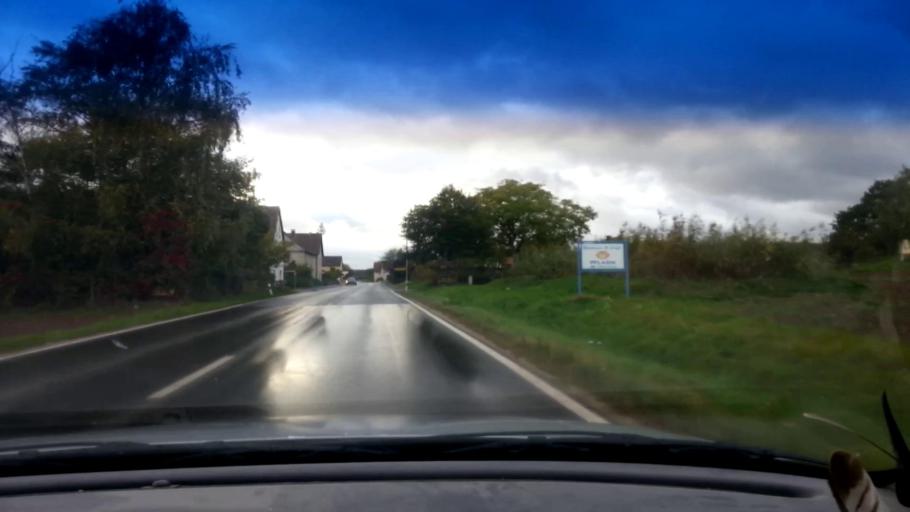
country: DE
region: Bavaria
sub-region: Upper Franconia
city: Burgwindheim
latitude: 49.8217
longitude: 10.6537
